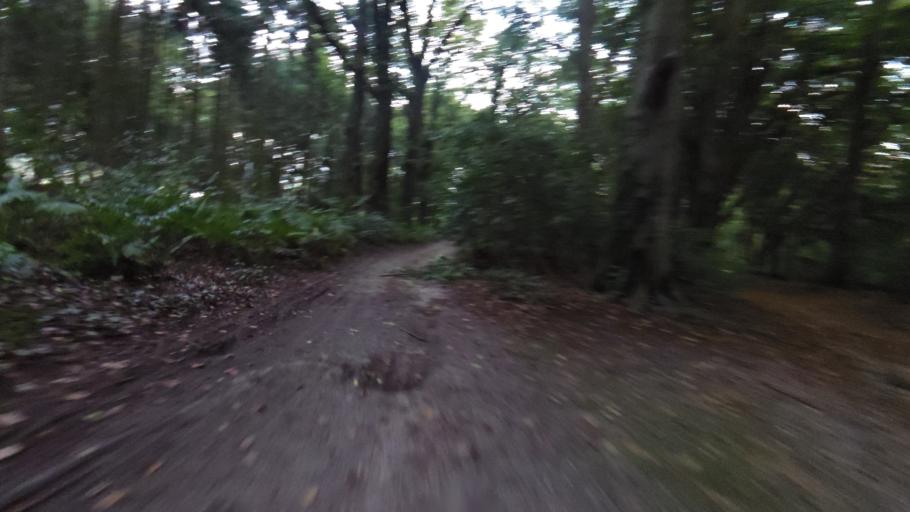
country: NL
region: Gelderland
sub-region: Gemeente Renkum
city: Doorwerth
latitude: 51.9830
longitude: 5.8165
